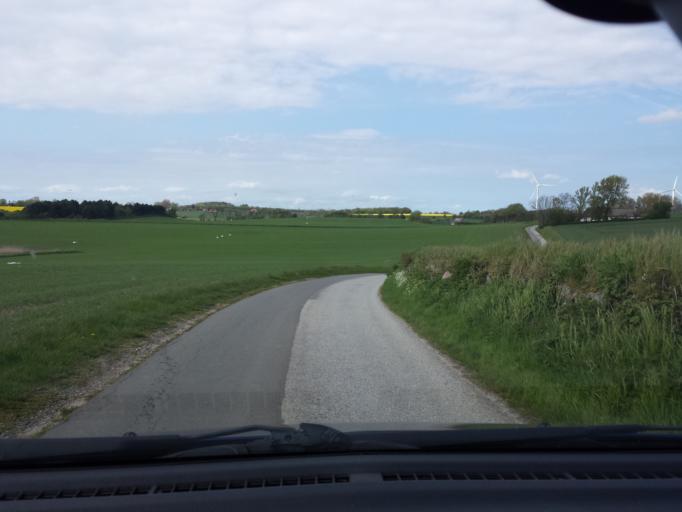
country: DK
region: South Denmark
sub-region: Langeland Kommune
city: Rudkobing
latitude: 54.8051
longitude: 10.6868
